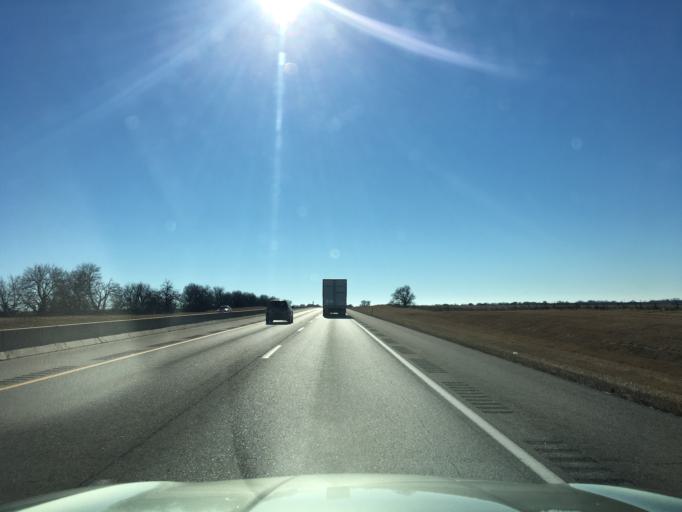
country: US
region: Kansas
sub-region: Sumner County
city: Wellington
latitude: 37.1113
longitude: -97.3388
